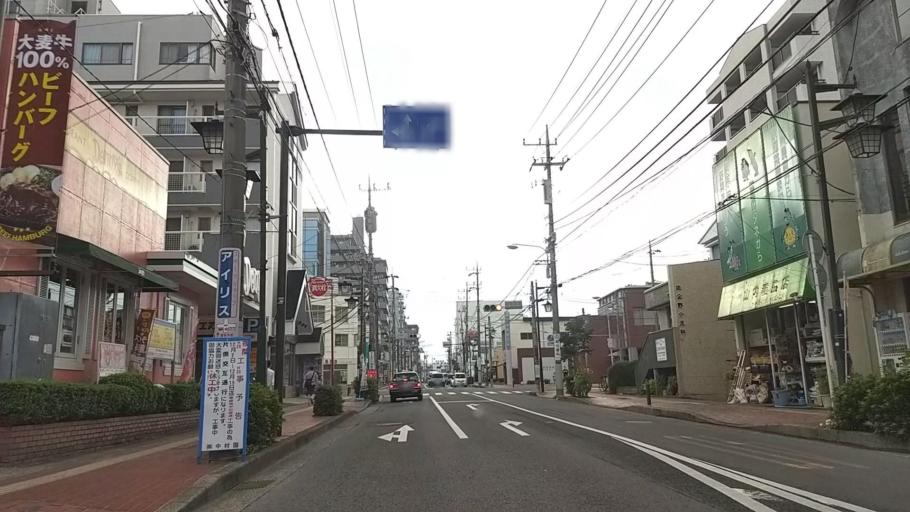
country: JP
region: Kanagawa
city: Isehara
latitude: 35.3974
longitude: 139.3091
